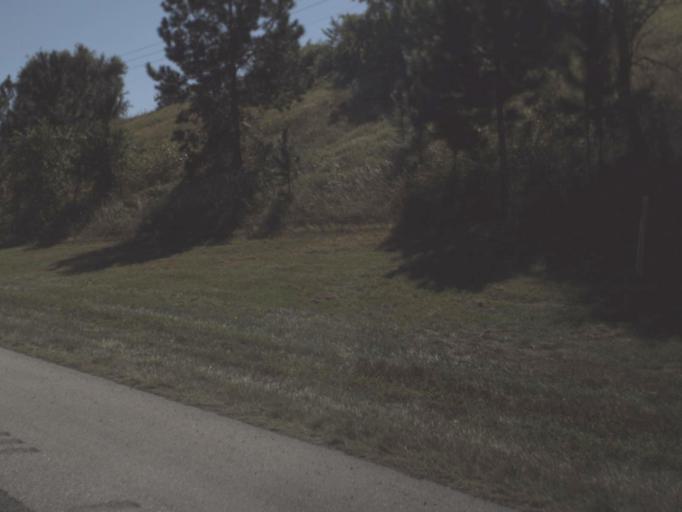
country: US
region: Florida
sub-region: Lake County
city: Montverde
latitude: 28.5723
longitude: -81.6966
